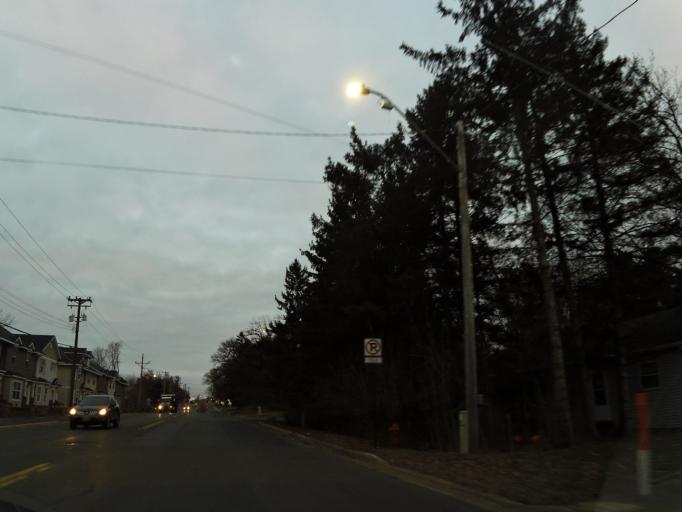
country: US
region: Minnesota
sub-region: Washington County
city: Mahtomedi
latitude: 45.0571
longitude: -92.9540
